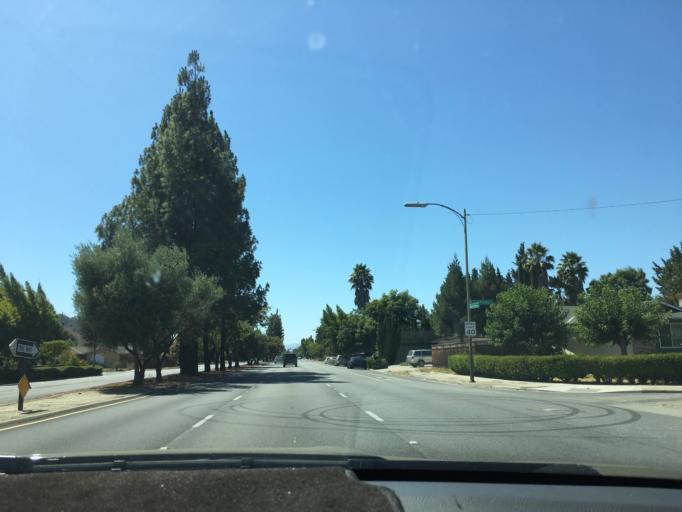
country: US
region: California
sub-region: Santa Clara County
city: Seven Trees
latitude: 37.2378
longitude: -121.8461
